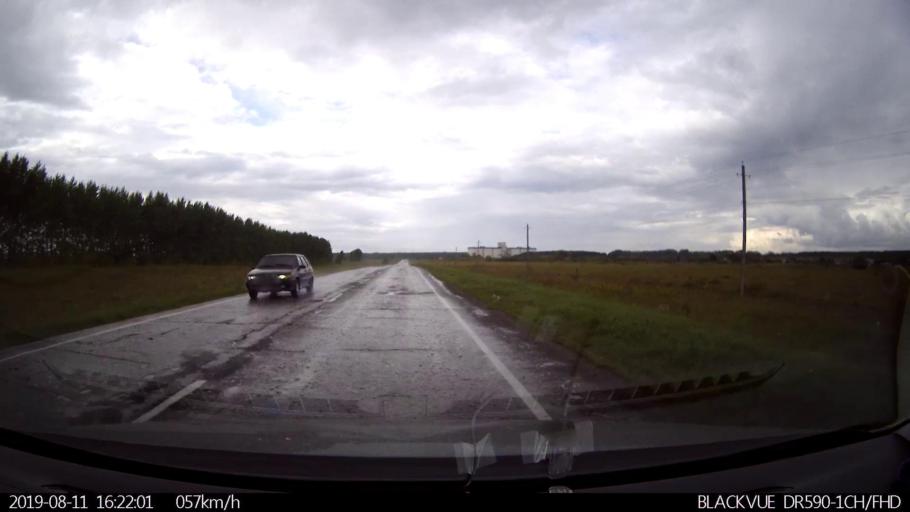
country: RU
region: Ulyanovsk
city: Mayna
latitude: 54.0844
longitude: 47.5951
